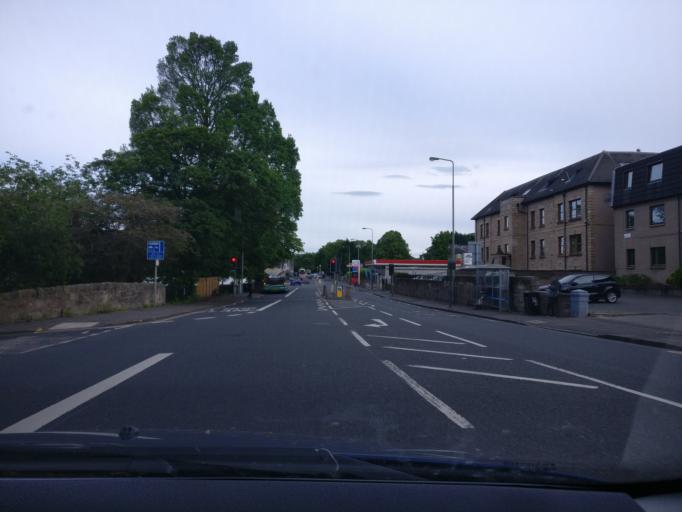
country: GB
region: Scotland
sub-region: West Lothian
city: Seafield
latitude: 55.9480
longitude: -3.1379
